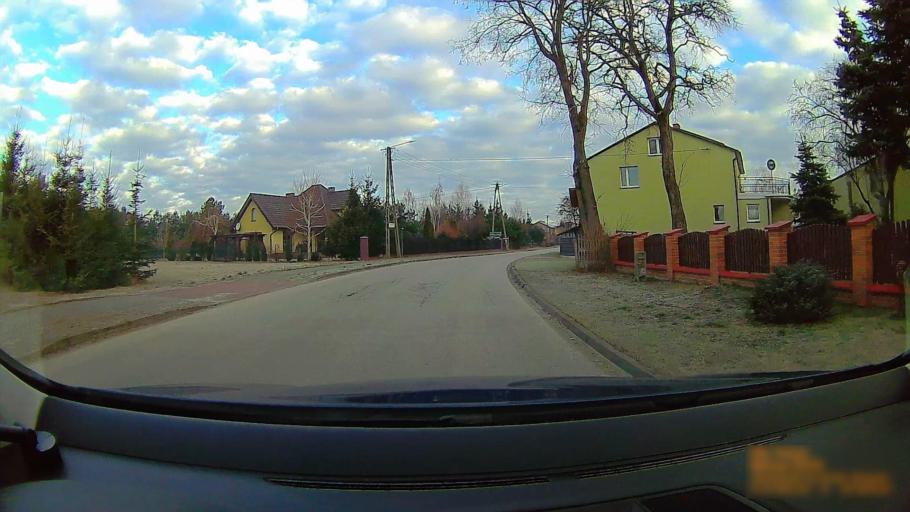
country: PL
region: Greater Poland Voivodeship
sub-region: Powiat koninski
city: Rzgow Pierwszy
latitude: 52.1503
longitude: 18.0526
